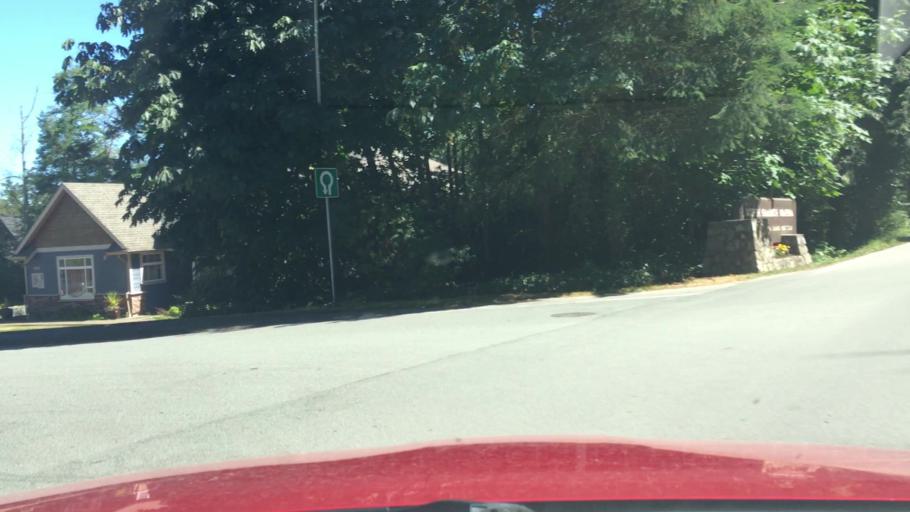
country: CA
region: British Columbia
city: North Saanich
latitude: 48.6747
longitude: -123.4241
